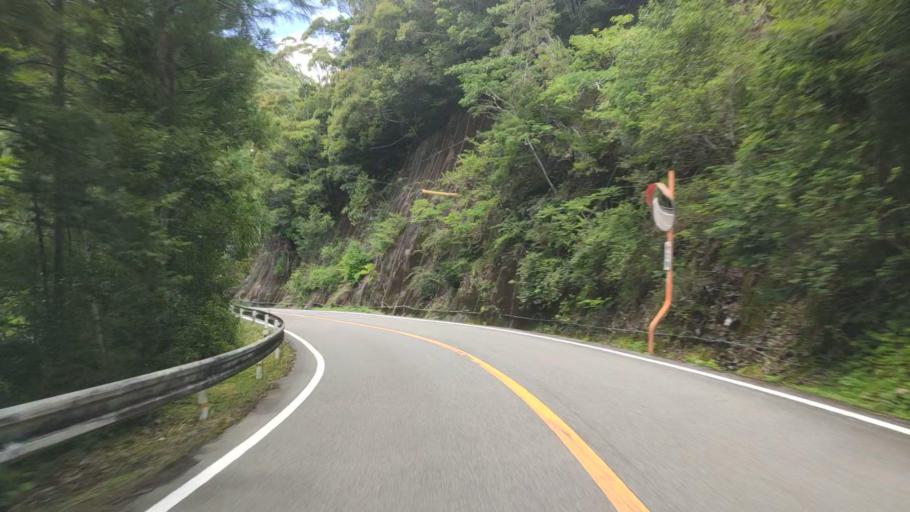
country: JP
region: Mie
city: Owase
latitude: 34.0013
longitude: 136.0092
